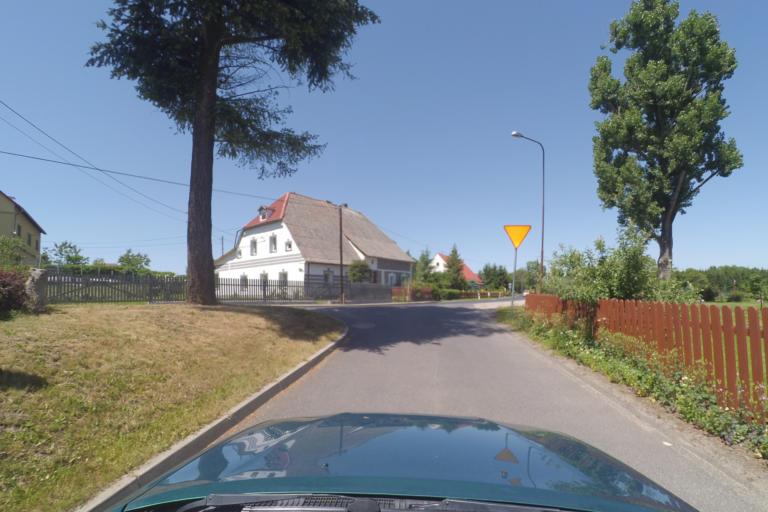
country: PL
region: Lower Silesian Voivodeship
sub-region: Powiat kamiennogorski
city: Krzeszow
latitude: 50.7348
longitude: 16.0689
